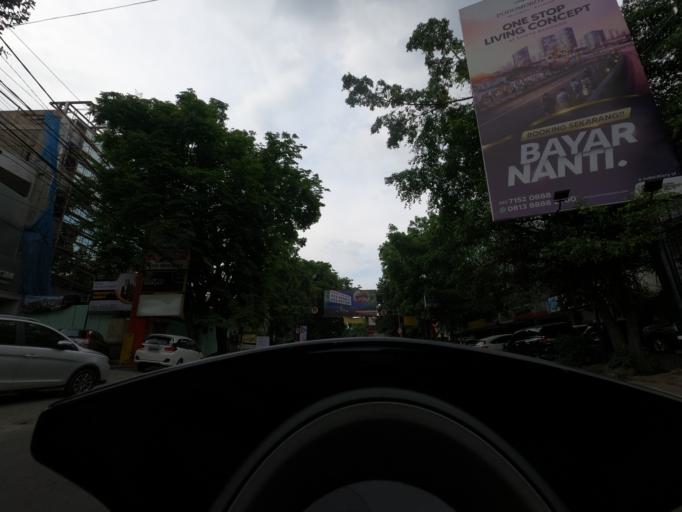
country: ID
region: West Java
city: Bandung
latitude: -6.9193
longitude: 107.6179
